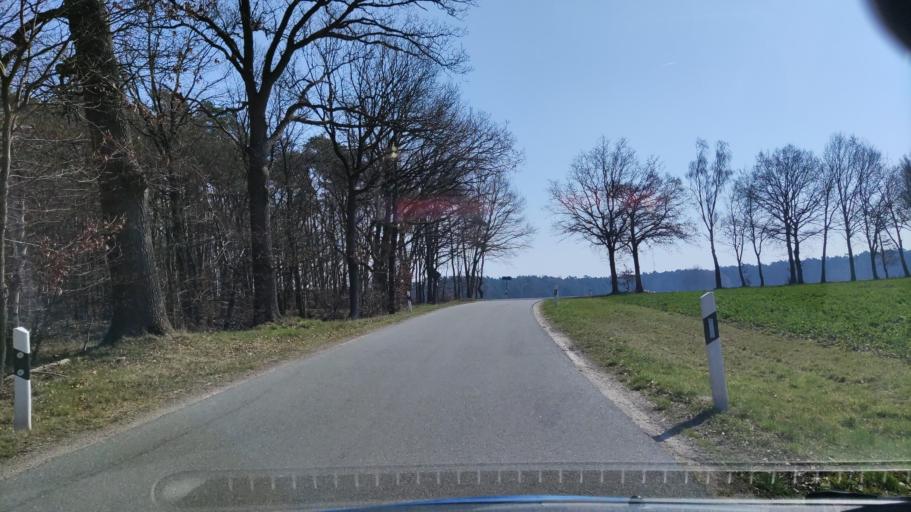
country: DE
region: Lower Saxony
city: Clenze
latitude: 52.9789
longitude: 10.8873
